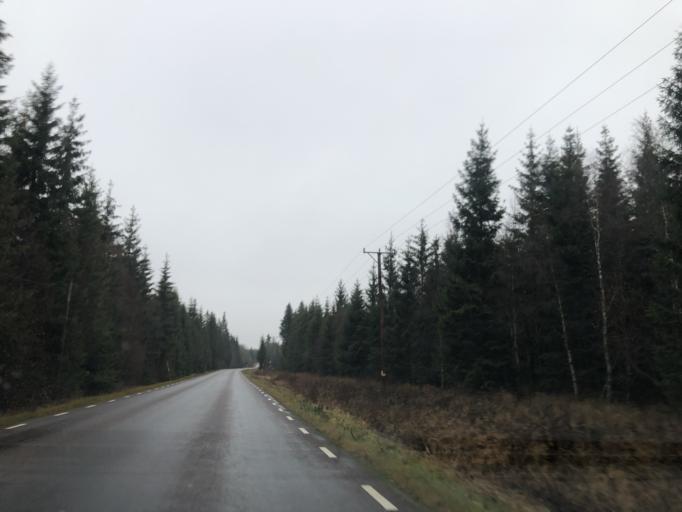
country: SE
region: Vaestra Goetaland
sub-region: Ulricehamns Kommun
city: Ulricehamn
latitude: 57.7485
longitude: 13.5254
